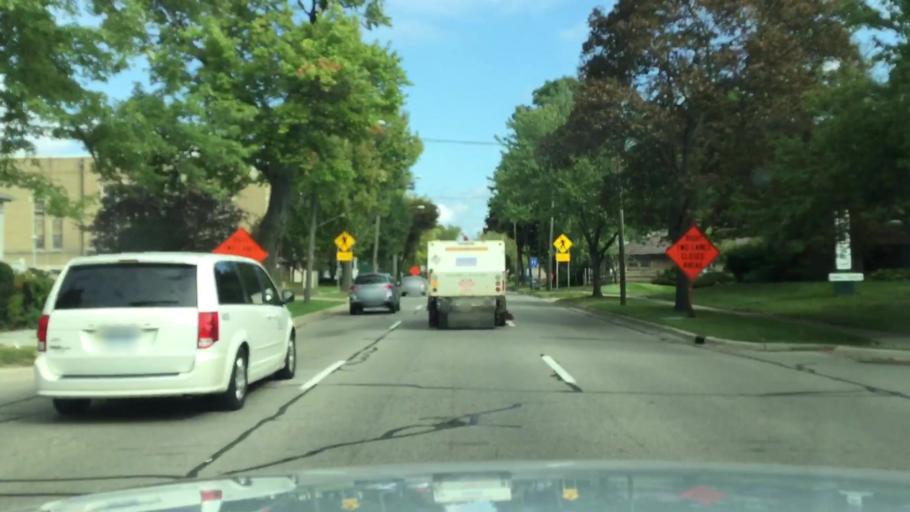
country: US
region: Michigan
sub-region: Kalamazoo County
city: Kalamazoo
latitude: 42.2851
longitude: -85.5873
